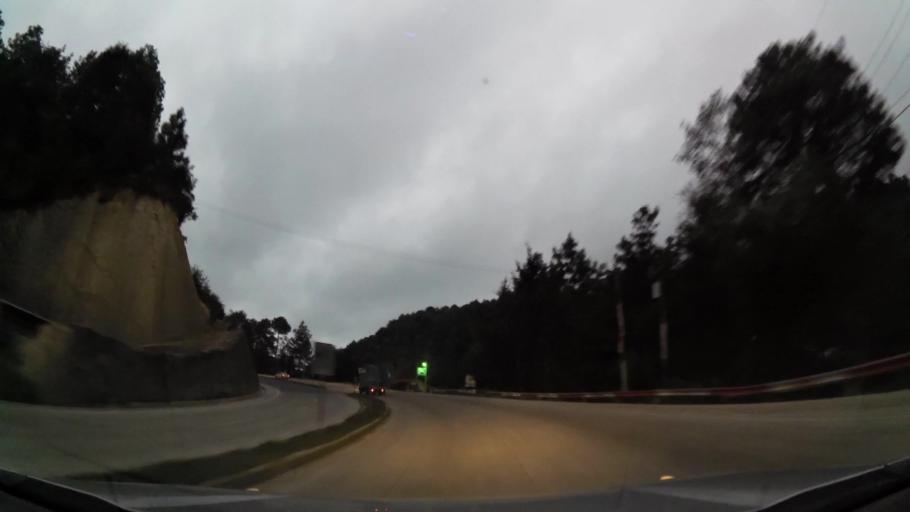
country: GT
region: Chimaltenango
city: Santa Apolonia
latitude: 14.8220
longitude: -91.0272
